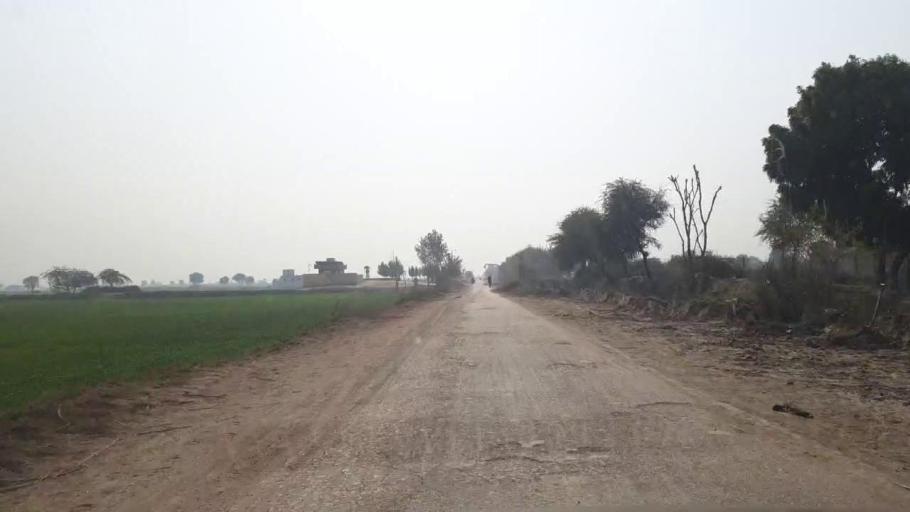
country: PK
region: Sindh
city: Hala
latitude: 25.9119
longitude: 68.4459
